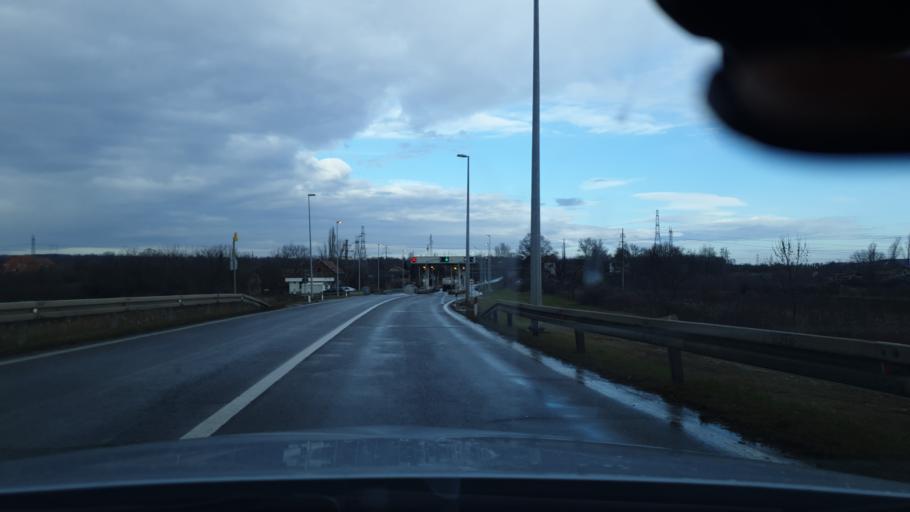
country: RS
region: Central Serbia
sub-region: Podunavski Okrug
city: Smederevo
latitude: 44.5889
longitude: 20.9577
